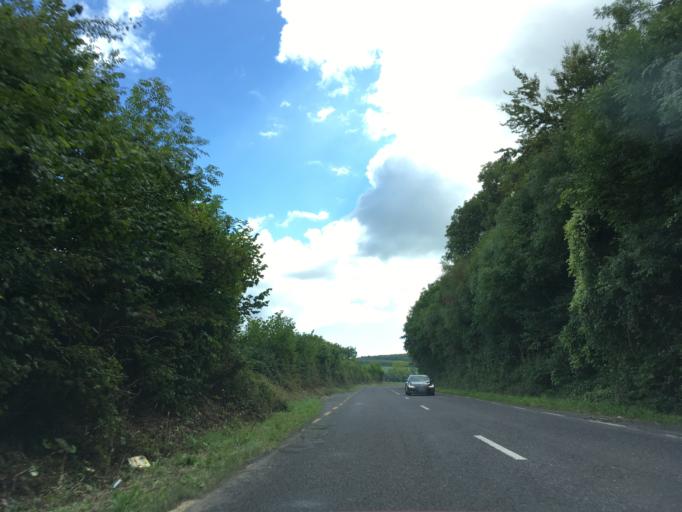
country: IE
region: Munster
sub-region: County Cork
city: Carrigaline
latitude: 51.8099
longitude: -8.3524
